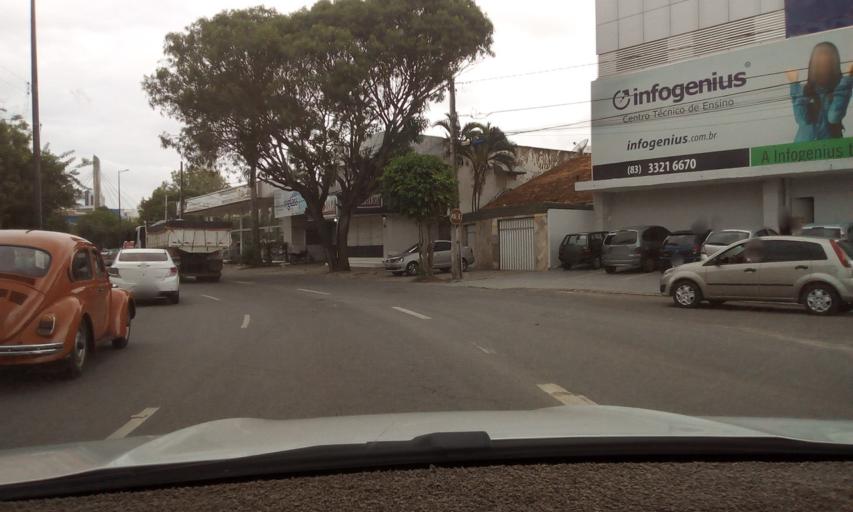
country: BR
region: Paraiba
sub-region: Campina Grande
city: Campina Grande
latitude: -7.2200
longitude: -35.8748
